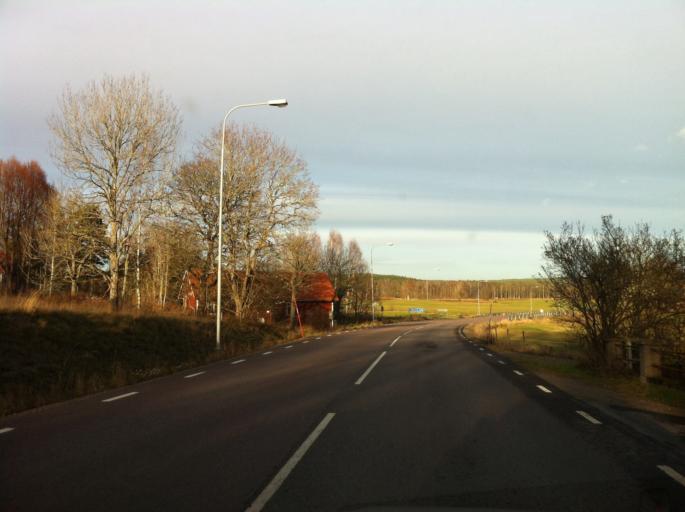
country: SE
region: Kalmar
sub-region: Hultsfreds Kommun
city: Virserum
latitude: 57.3985
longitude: 15.6034
